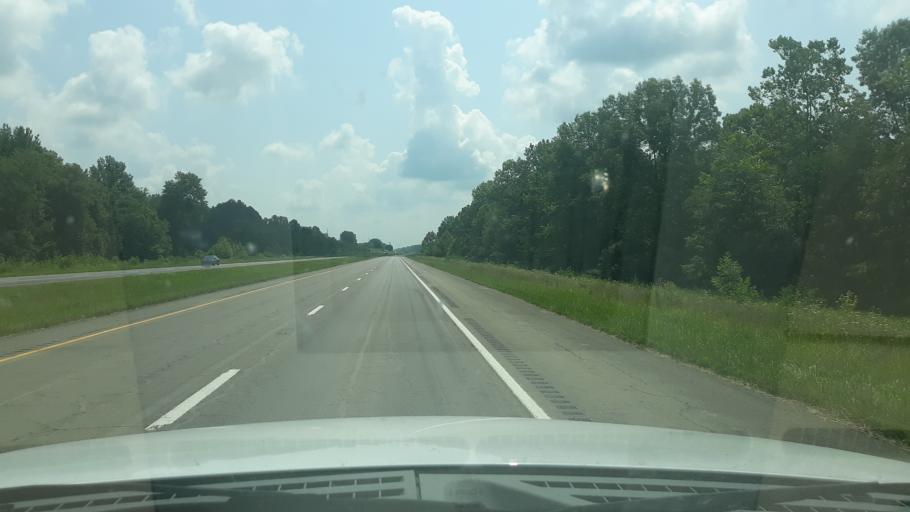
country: US
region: Illinois
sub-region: Saline County
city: Carrier Mills
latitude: 37.7341
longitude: -88.6870
